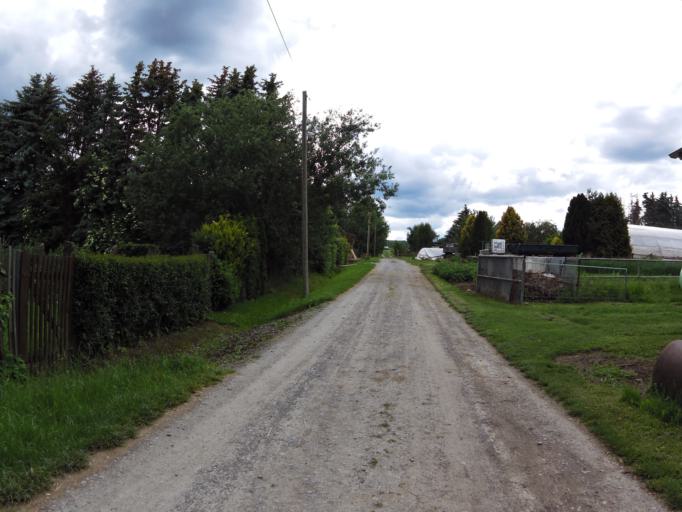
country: DE
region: Thuringia
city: Langula
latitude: 51.1524
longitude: 10.4155
